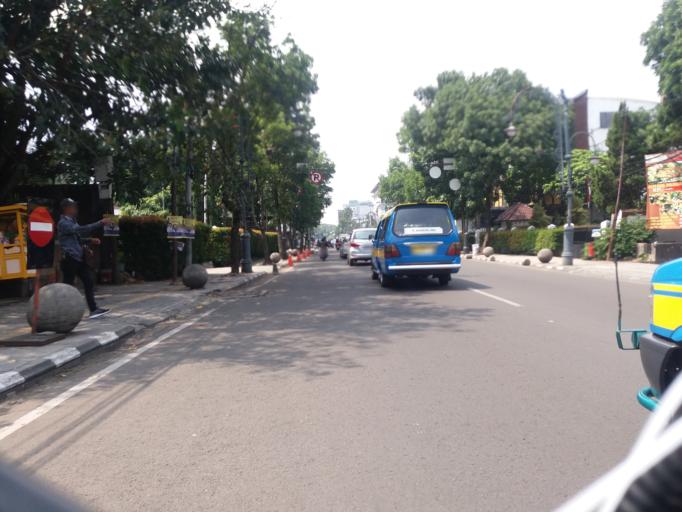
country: ID
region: West Java
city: Bandung
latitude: -6.9064
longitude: 107.6145
